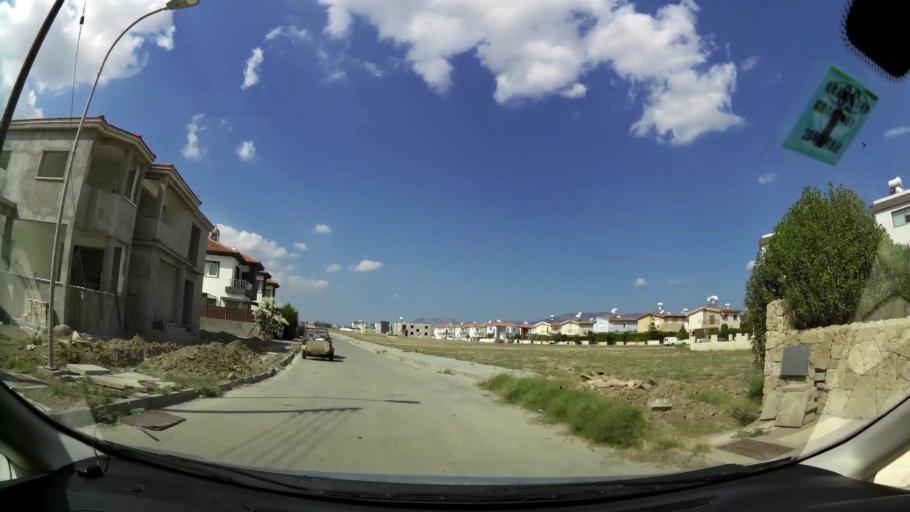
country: CY
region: Lefkosia
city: Nicosia
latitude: 35.2205
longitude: 33.2954
